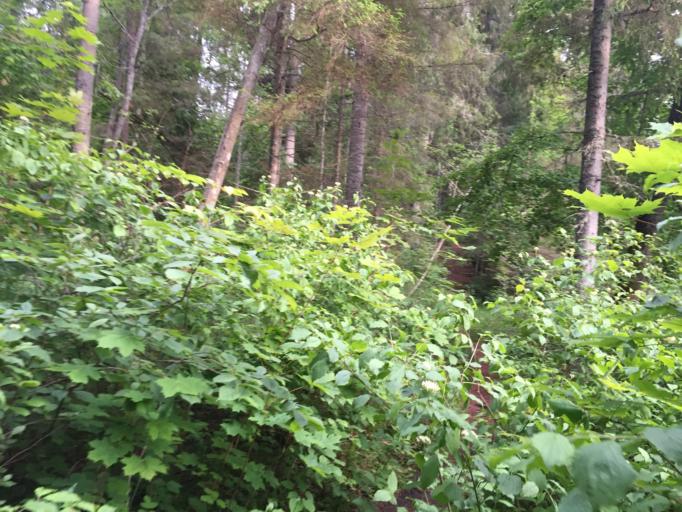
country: LV
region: Ligatne
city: Ligatne
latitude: 57.2300
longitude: 25.1519
